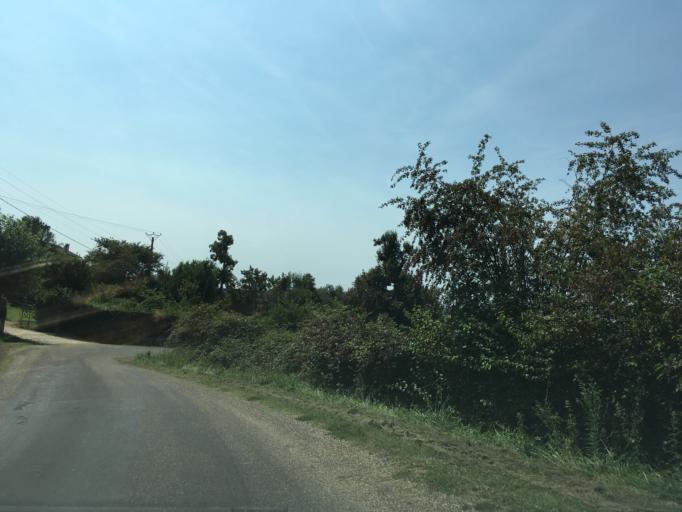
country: FR
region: Midi-Pyrenees
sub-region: Departement du Tarn-et-Garonne
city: Saint-Nauphary
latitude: 43.9902
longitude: 1.4011
